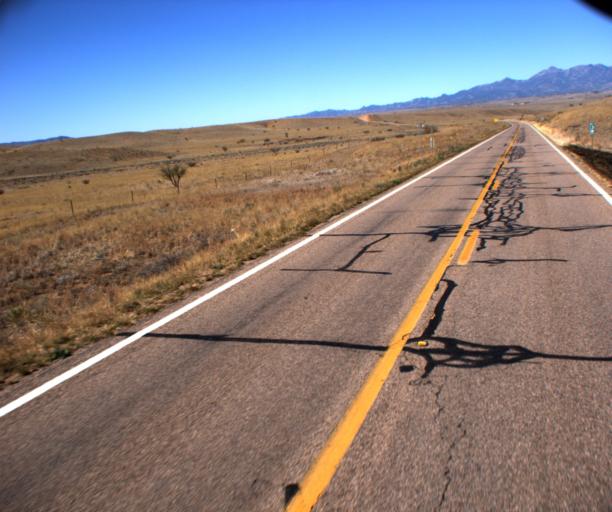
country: US
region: Arizona
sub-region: Cochise County
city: Huachuca City
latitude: 31.7106
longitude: -110.5686
